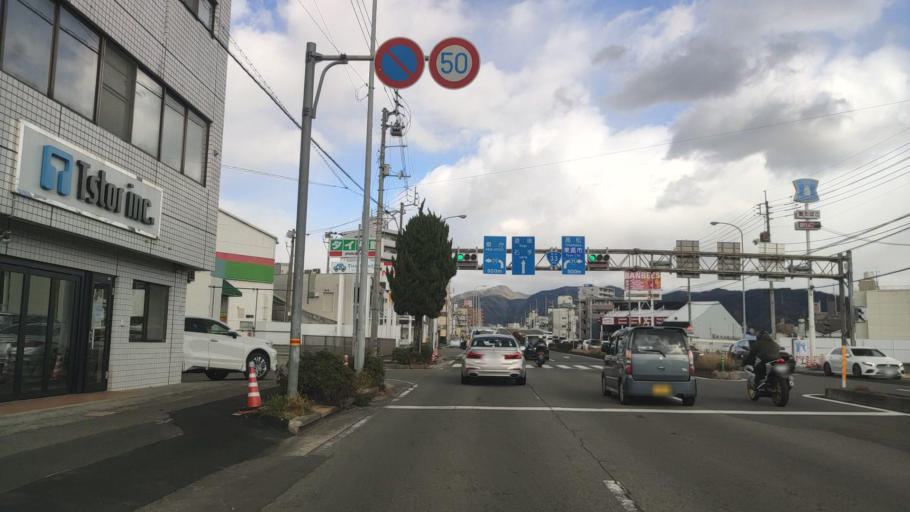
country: JP
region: Ehime
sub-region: Shikoku-chuo Shi
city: Matsuyama
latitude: 33.8235
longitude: 132.7785
